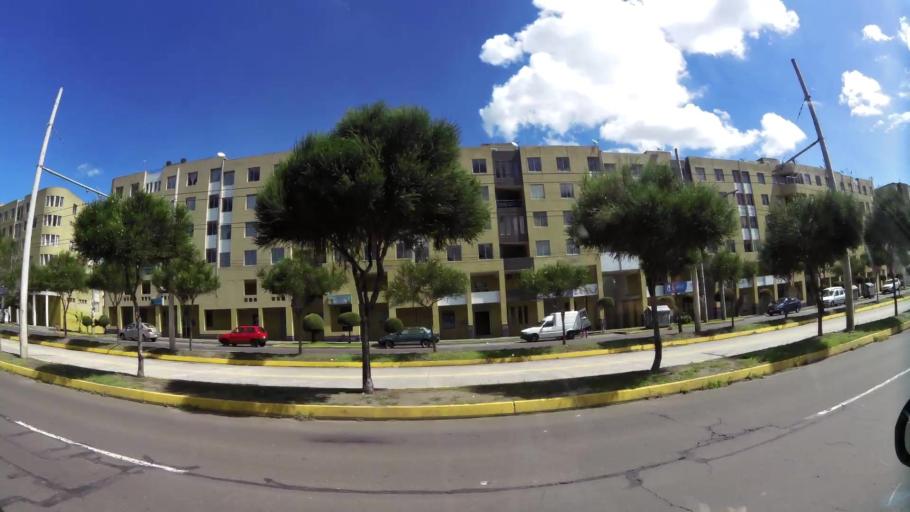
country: EC
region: Pichincha
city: Quito
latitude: -0.2926
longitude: -78.5467
